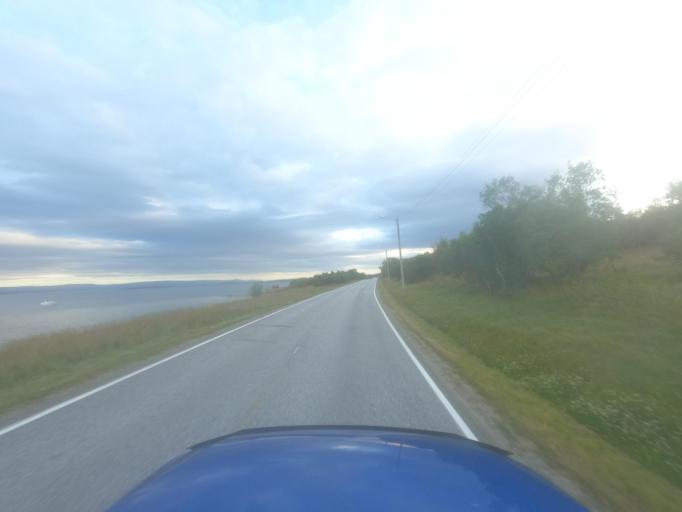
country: NO
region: Finnmark Fylke
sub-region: Porsanger
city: Lakselv
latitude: 70.4548
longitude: 25.2256
